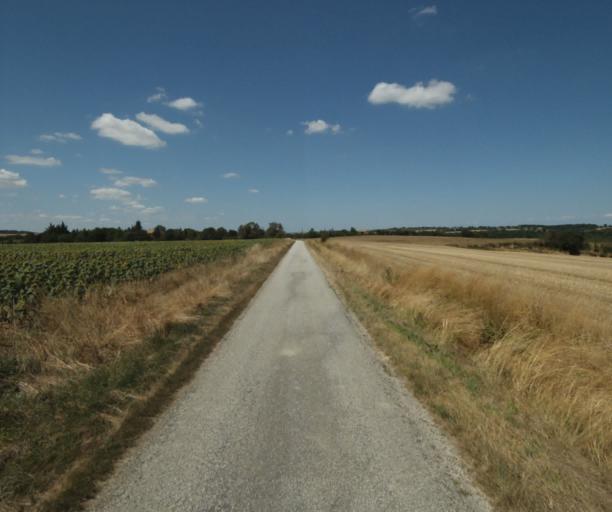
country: FR
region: Midi-Pyrenees
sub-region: Departement de la Haute-Garonne
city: Auriac-sur-Vendinelle
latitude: 43.4969
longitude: 1.8530
